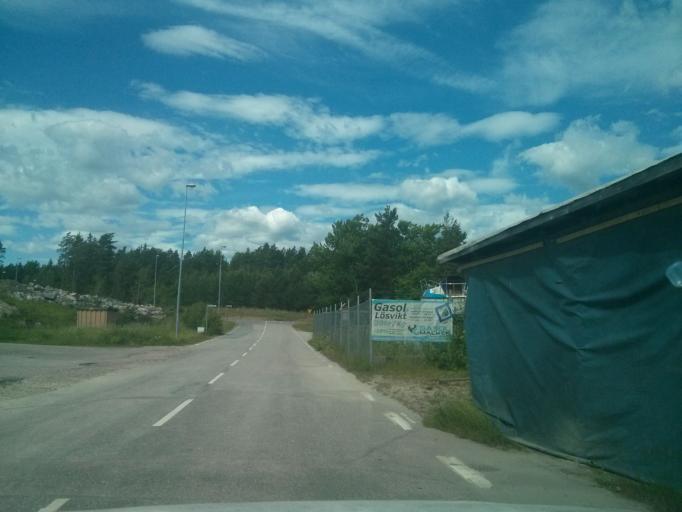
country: SE
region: Soedermanland
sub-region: Oxelosunds Kommun
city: Oxelosund
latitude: 58.6565
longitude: 17.1060
